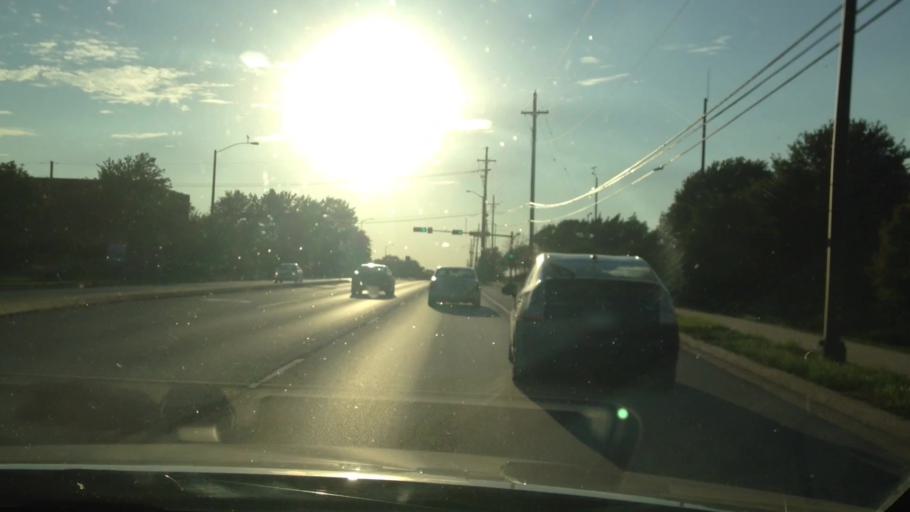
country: US
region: Kansas
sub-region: Johnson County
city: Lenexa
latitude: 38.9711
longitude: -94.7317
